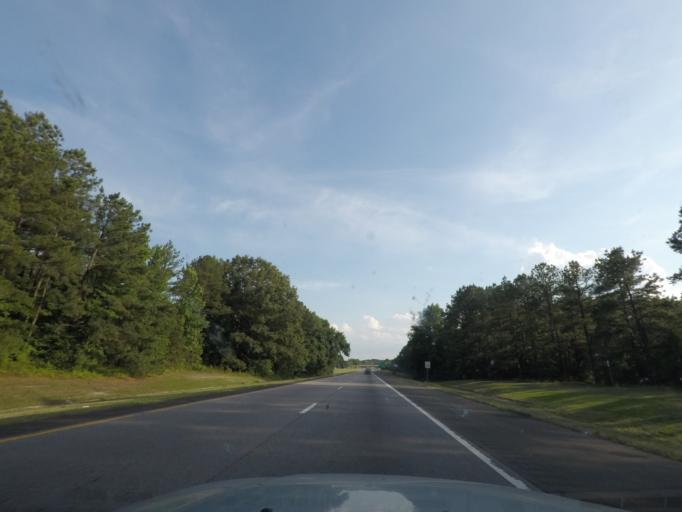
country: US
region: North Carolina
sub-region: Granville County
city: Butner
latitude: 36.0868
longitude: -78.7636
